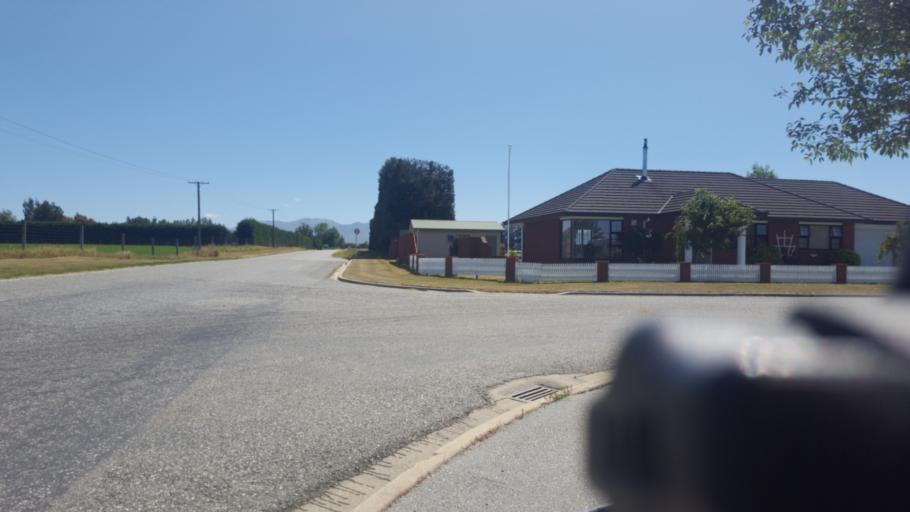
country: NZ
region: Otago
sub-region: Dunedin City
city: Dunedin
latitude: -45.1249
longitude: 170.1062
